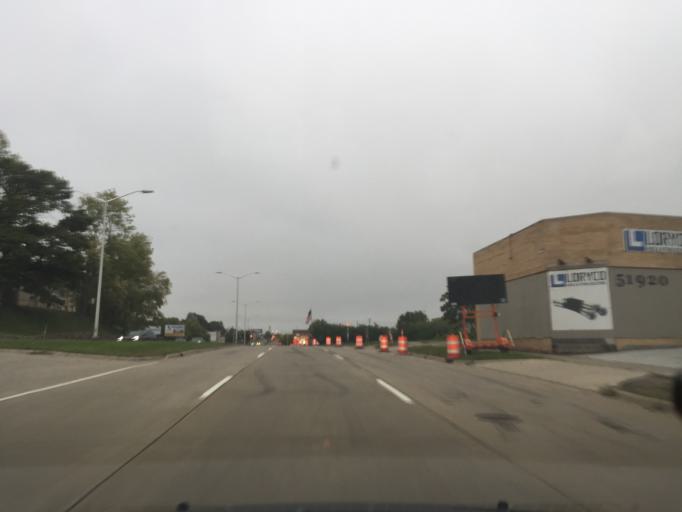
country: US
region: Michigan
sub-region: Oakland County
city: Pontiac
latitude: 42.6298
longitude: -83.2892
